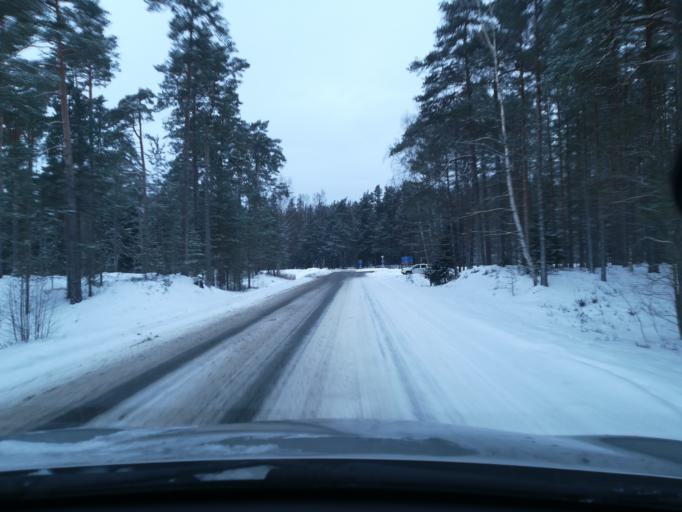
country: EE
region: Harju
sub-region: Keila linn
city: Keila
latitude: 59.3918
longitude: 24.2942
